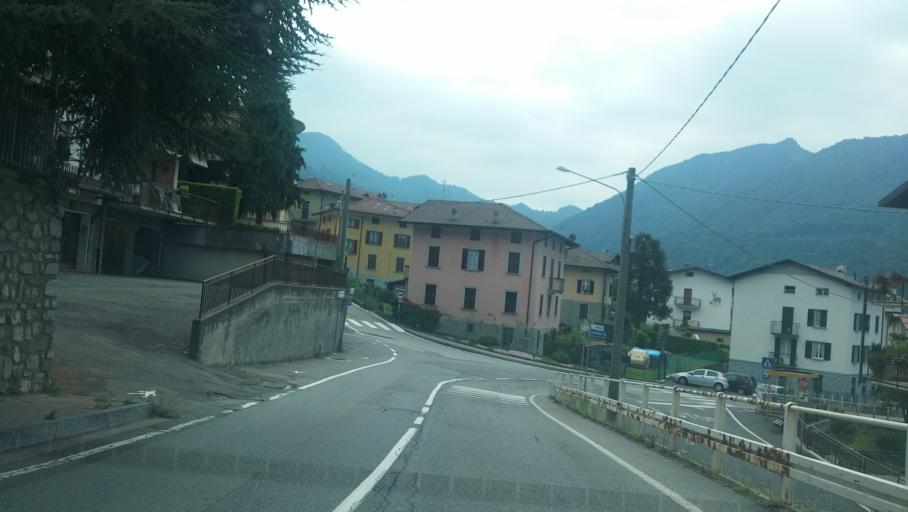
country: IT
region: Lombardy
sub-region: Provincia di Lecco
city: Cassina Valsassina
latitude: 45.9336
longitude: 9.4780
